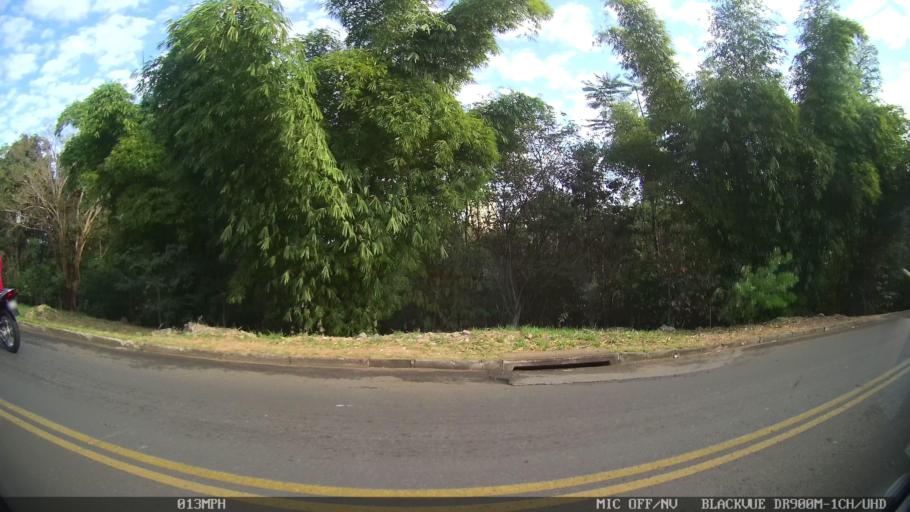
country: BR
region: Sao Paulo
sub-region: Americana
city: Americana
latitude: -22.7368
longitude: -47.3463
